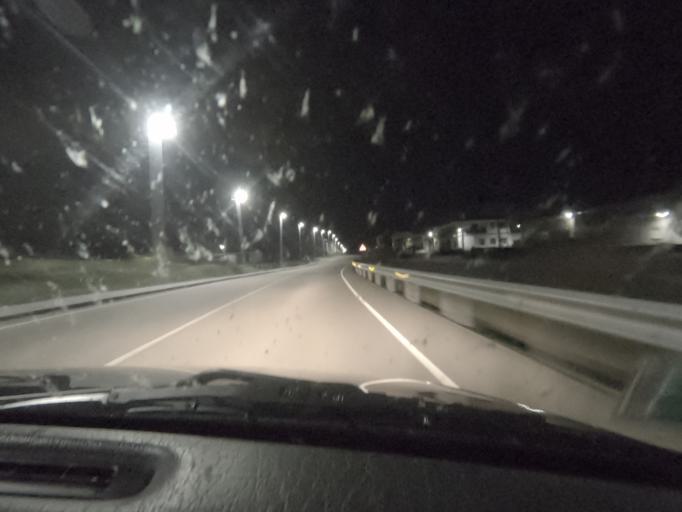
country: ES
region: Castille and Leon
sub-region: Provincia de Salamanca
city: Robleda
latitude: 40.3856
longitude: -6.6091
